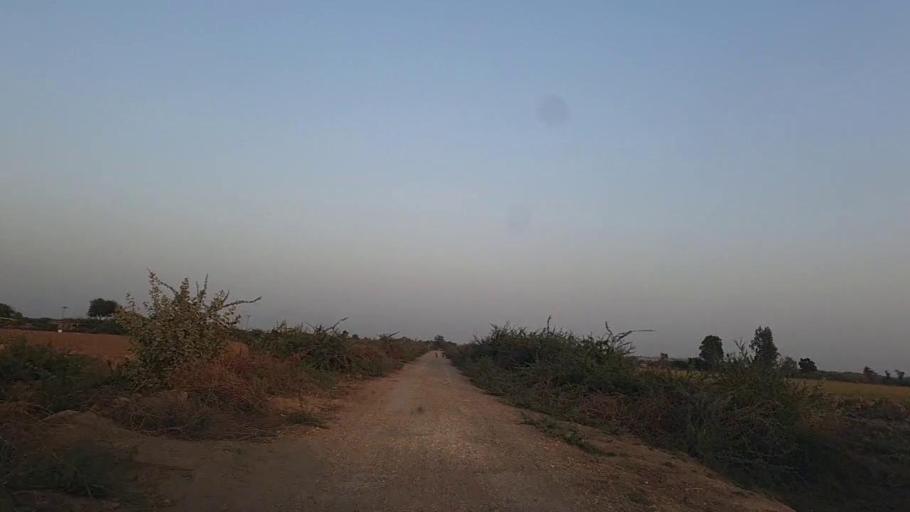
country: PK
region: Sindh
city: Naukot
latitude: 24.6949
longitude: 69.2808
